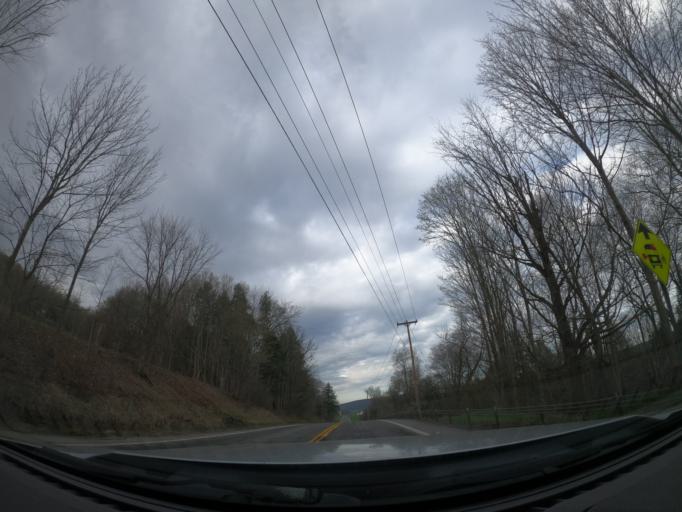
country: US
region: New York
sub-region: Madison County
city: Cazenovia
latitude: 42.7931
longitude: -75.8644
